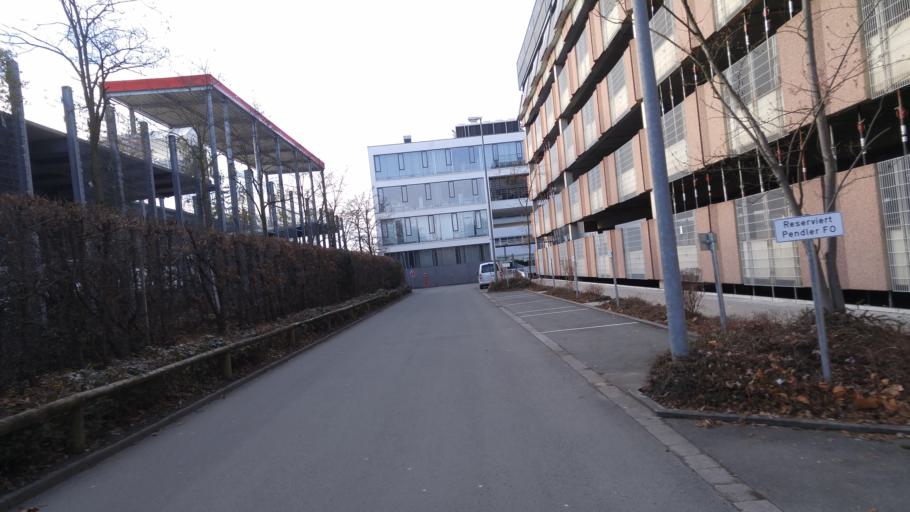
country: DE
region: Bavaria
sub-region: Regierungsbezirk Mittelfranken
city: Erlangen
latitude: 49.5934
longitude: 11.0251
